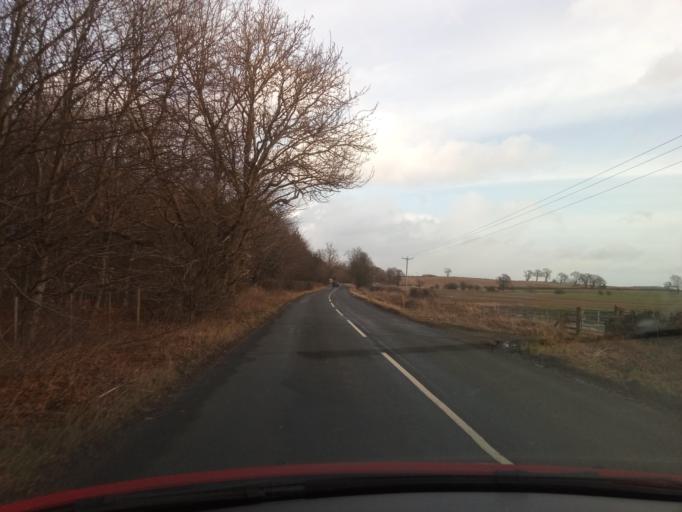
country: GB
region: England
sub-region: Northumberland
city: Rothley
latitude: 55.1359
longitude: -1.9744
